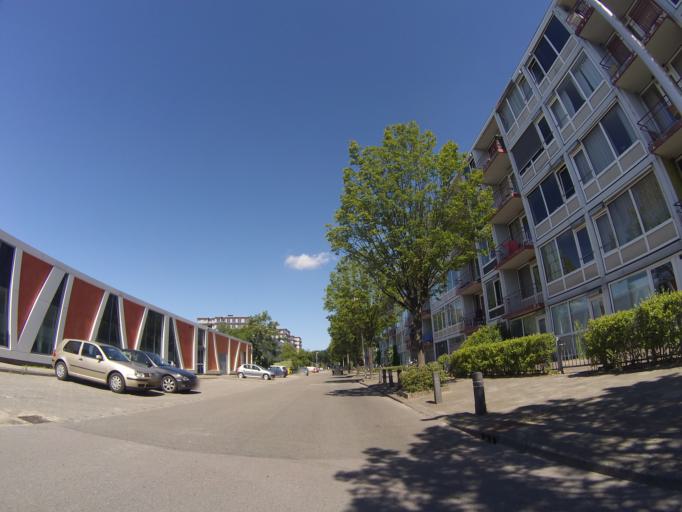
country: NL
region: Utrecht
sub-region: Gemeente Utrecht
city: Utrecht
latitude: 52.1086
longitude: 5.1156
